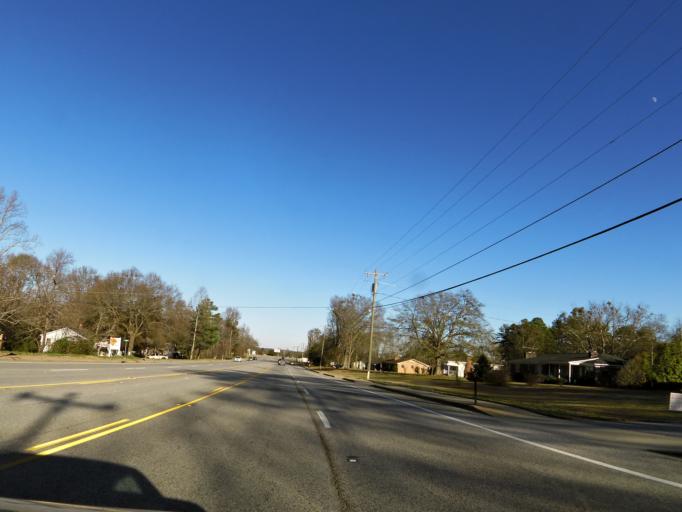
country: US
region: South Carolina
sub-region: Spartanburg County
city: Wellford
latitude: 34.8875
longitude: -82.0633
